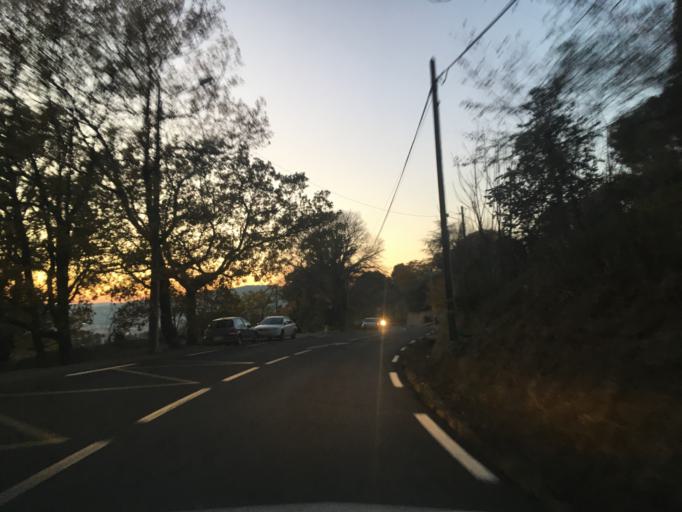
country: FR
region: Provence-Alpes-Cote d'Azur
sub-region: Departement du Var
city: Draguignan
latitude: 43.5378
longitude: 6.4784
